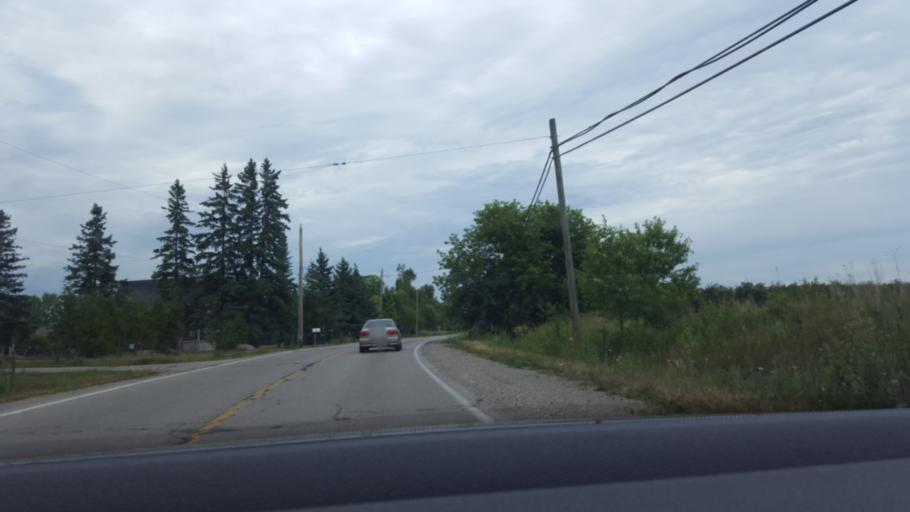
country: CA
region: Ontario
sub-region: Halton
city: Milton
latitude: 43.6036
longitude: -79.8515
